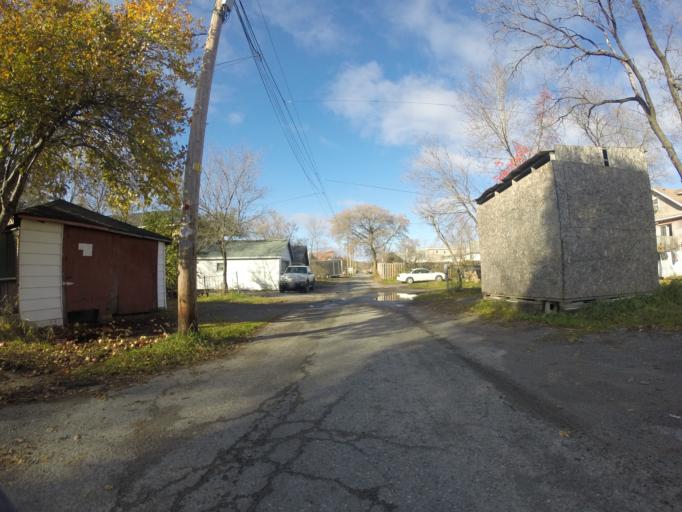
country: CA
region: Ontario
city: Greater Sudbury
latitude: 46.5012
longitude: -81.0064
